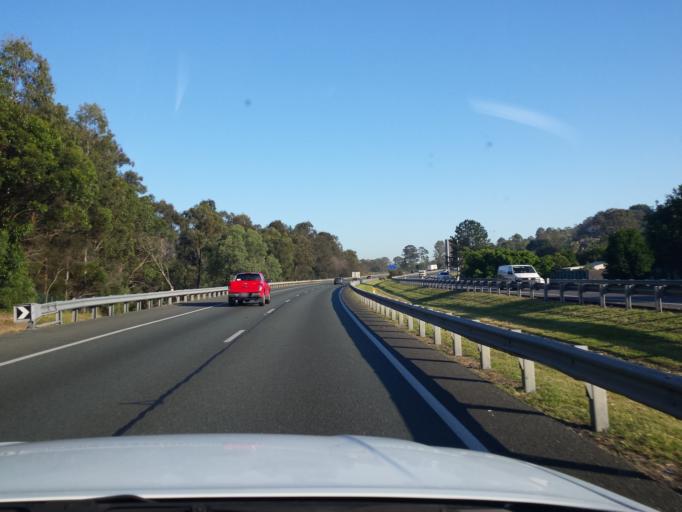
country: AU
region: Queensland
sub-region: Logan
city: Slacks Creek
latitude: -27.6781
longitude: 153.1682
